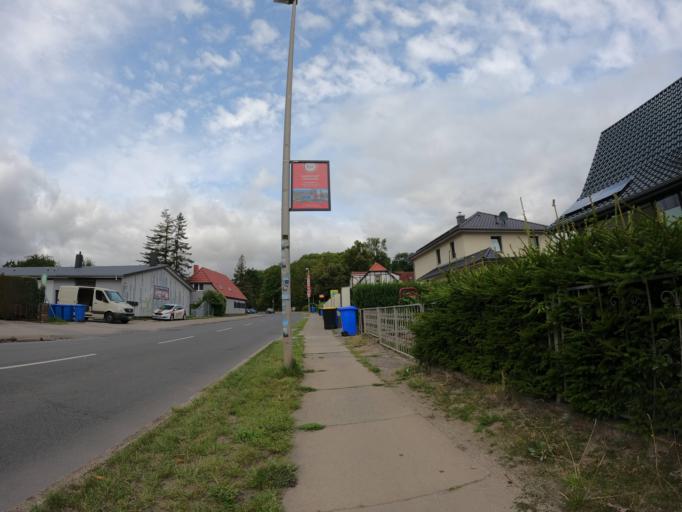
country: DE
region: Mecklenburg-Vorpommern
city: Stralsund
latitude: 54.3122
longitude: 13.0664
